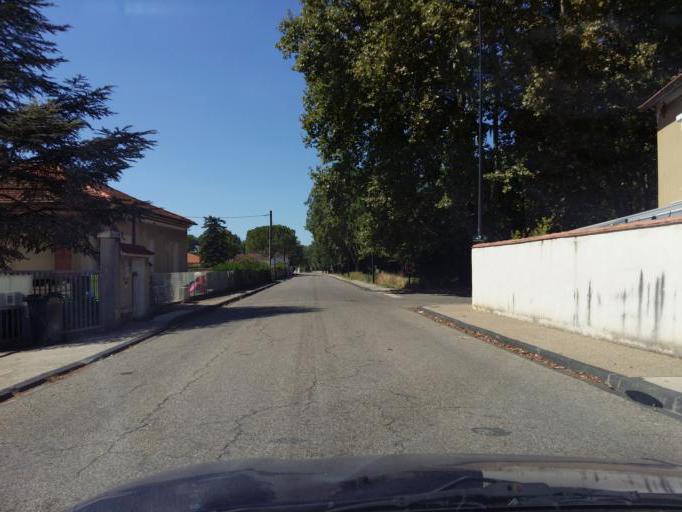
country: FR
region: Provence-Alpes-Cote d'Azur
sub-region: Departement du Vaucluse
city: Loriol-du-Comtat
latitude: 44.0743
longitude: 5.0047
